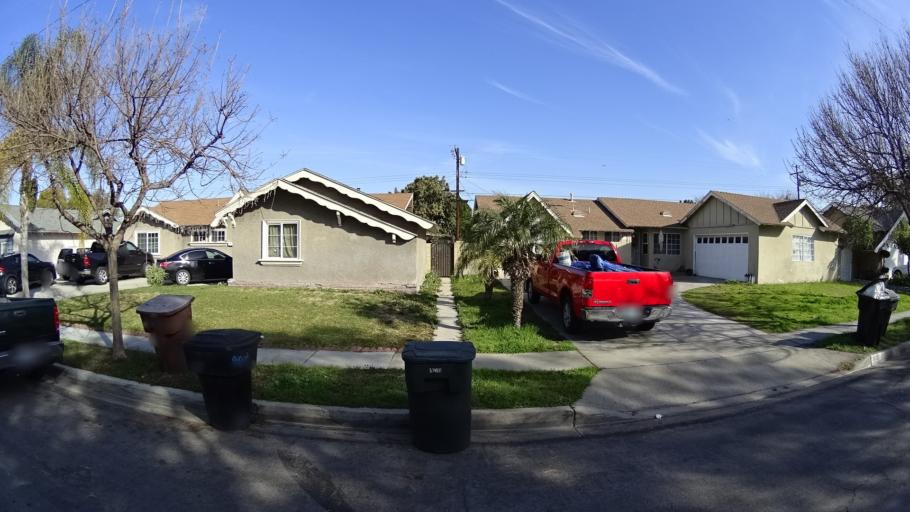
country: US
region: California
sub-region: Orange County
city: Fullerton
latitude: 33.8529
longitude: -117.9326
